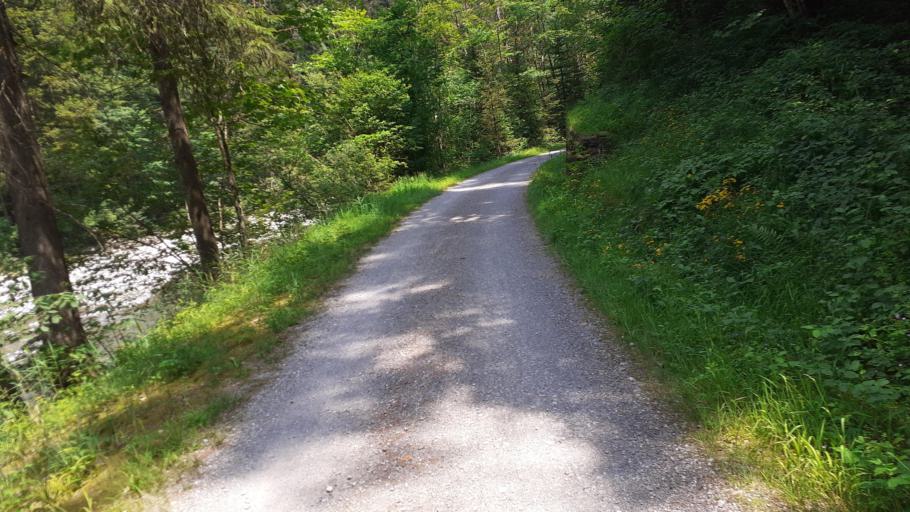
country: AT
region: Vorarlberg
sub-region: Politischer Bezirk Bregenz
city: Egg
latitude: 47.4439
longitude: 9.8892
